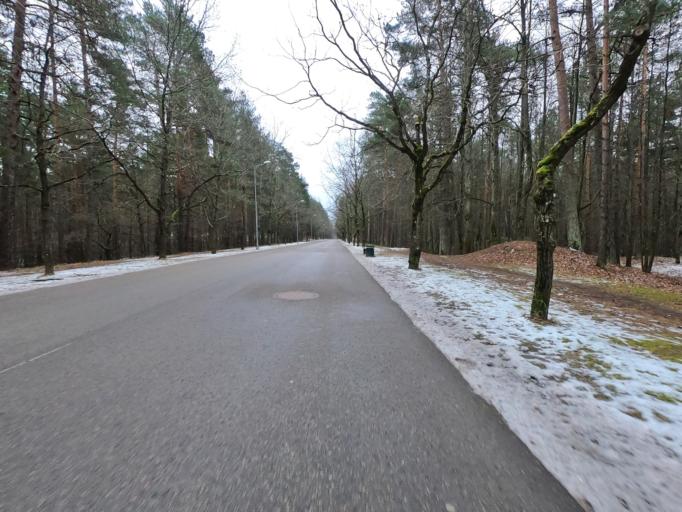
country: LV
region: Riga
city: Jaunciems
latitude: 57.0171
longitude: 24.1433
